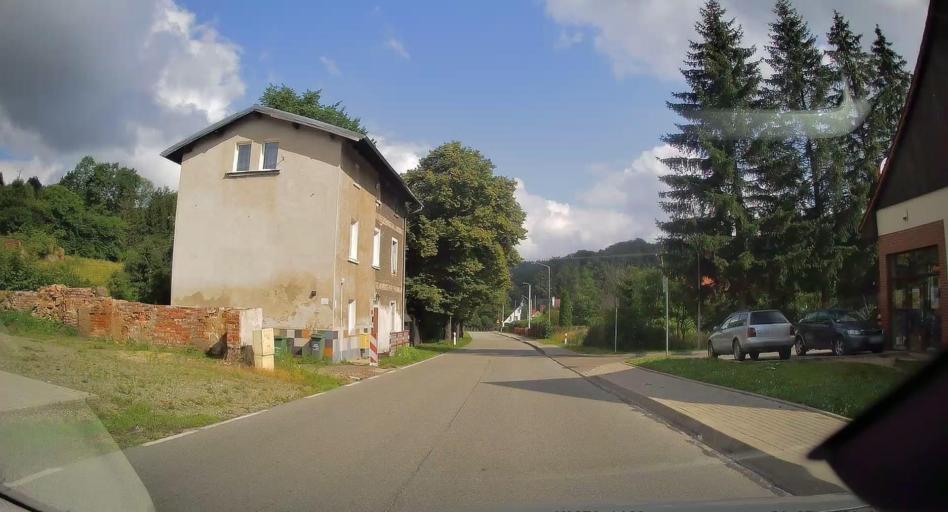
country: PL
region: Lower Silesian Voivodeship
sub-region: Powiat walbrzyski
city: Walim
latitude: 50.7041
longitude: 16.4381
